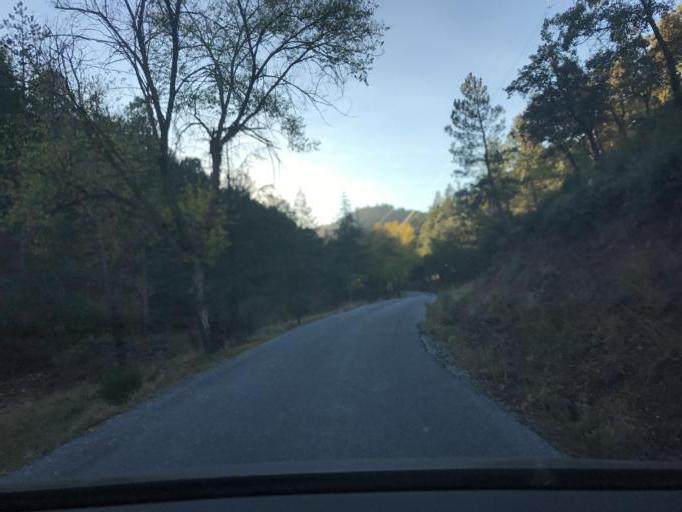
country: ES
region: Andalusia
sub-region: Provincia de Granada
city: Beas de Granada
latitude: 37.2905
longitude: -3.4916
